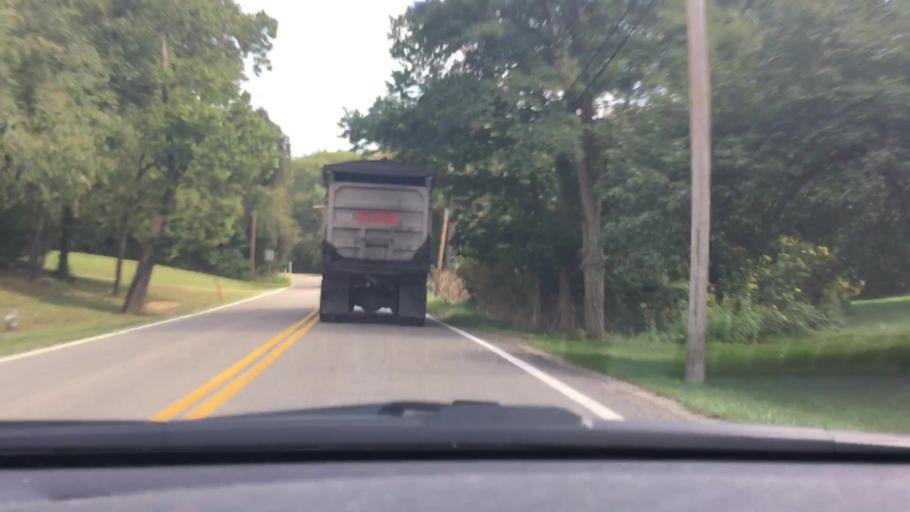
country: US
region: Pennsylvania
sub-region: Washington County
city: Gastonville
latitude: 40.2525
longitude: -79.9682
